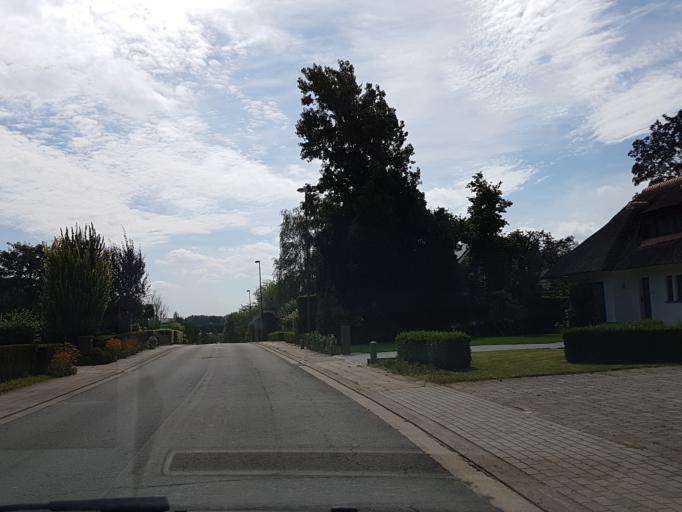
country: BE
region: Flanders
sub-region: Provincie Vlaams-Brabant
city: Herent
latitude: 50.8916
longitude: 4.6627
